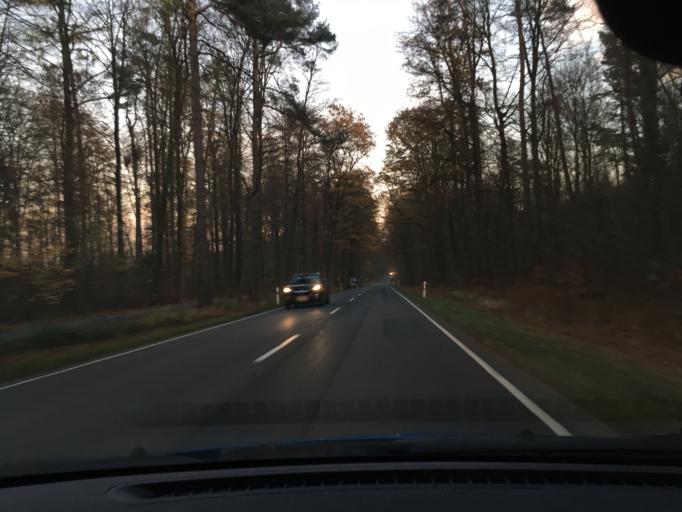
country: DE
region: Lower Saxony
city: Uelzen
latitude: 52.9796
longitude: 10.5340
